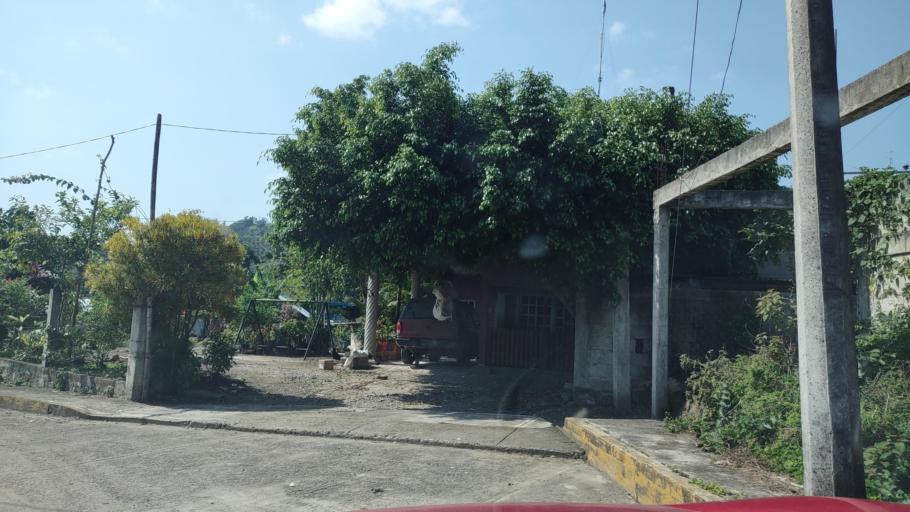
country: MX
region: Veracruz
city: Agua Dulce
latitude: 20.3112
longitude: -97.1747
